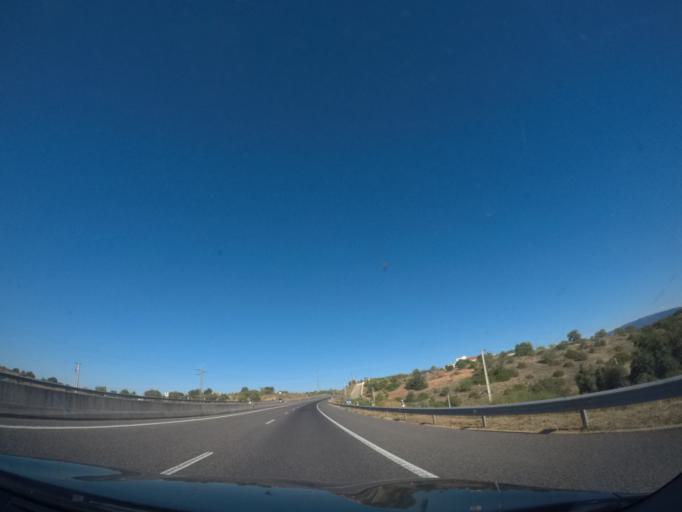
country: PT
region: Faro
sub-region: Lagoa
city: Estombar
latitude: 37.1567
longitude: -8.4832
